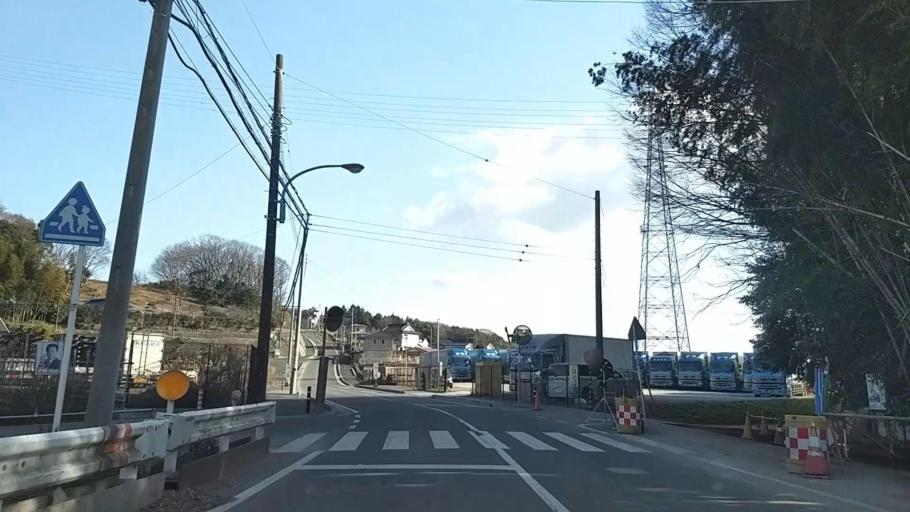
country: JP
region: Kanagawa
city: Atsugi
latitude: 35.4576
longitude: 139.3221
